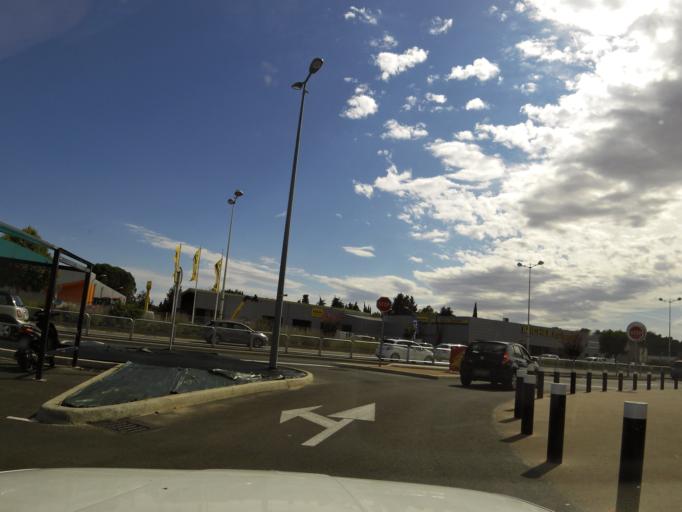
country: FR
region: Languedoc-Roussillon
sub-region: Departement du Gard
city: Ales
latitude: 44.1073
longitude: 4.0917
